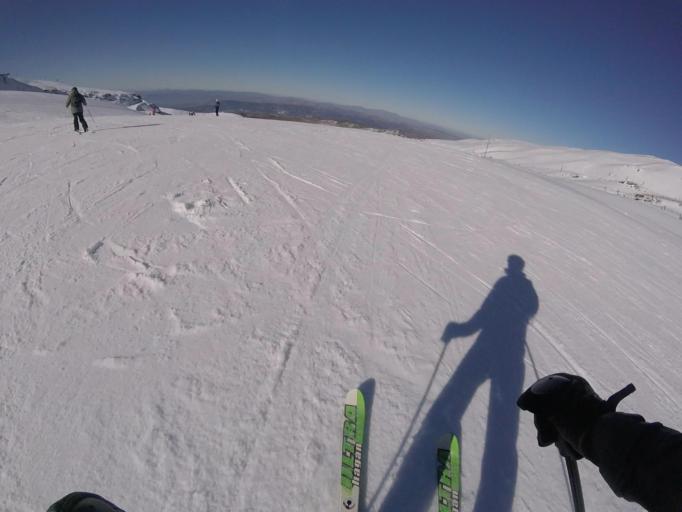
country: ES
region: Andalusia
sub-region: Provincia de Granada
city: Capileira
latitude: 37.0652
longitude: -3.3860
